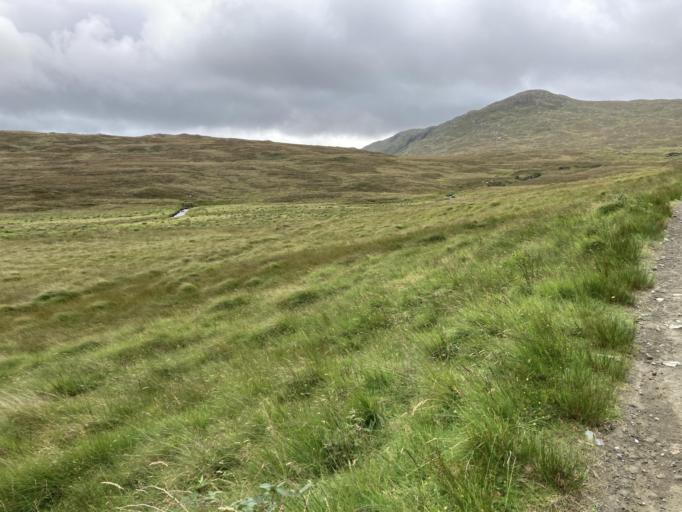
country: GB
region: Scotland
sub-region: Highland
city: Isle of Skye
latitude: 57.0230
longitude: -6.3464
